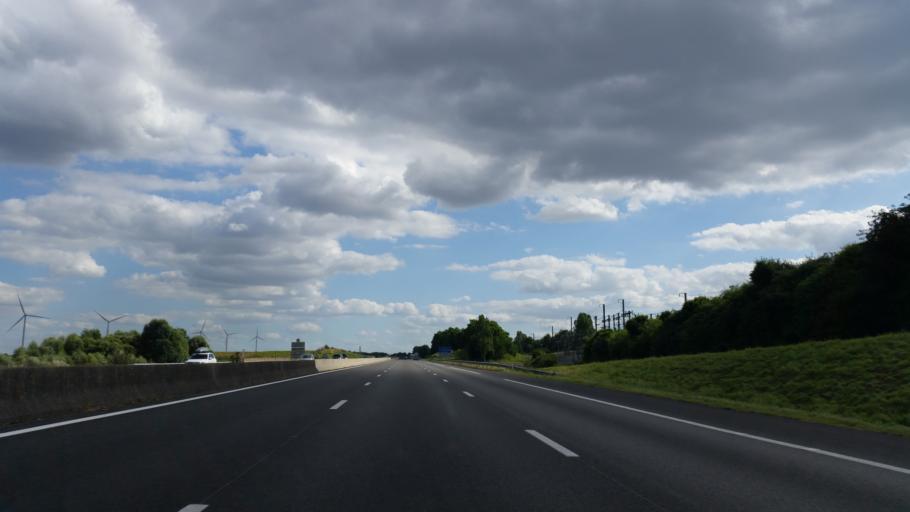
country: FR
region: Nord-Pas-de-Calais
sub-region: Departement du Pas-de-Calais
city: Bapaume
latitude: 50.0651
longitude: 2.8724
